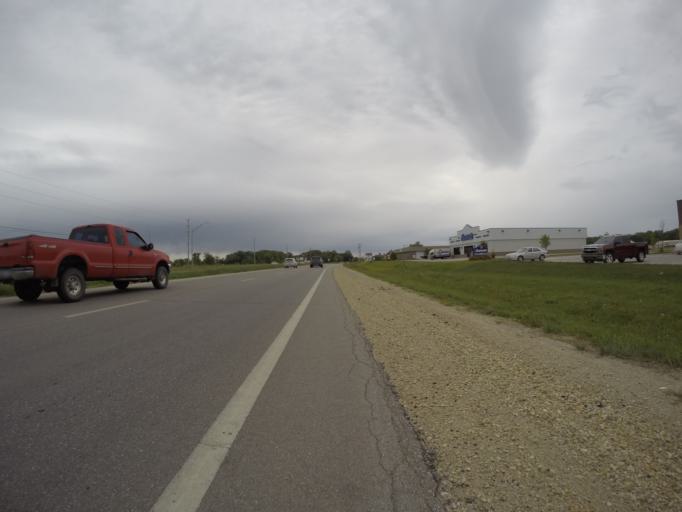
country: US
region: Kansas
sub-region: Riley County
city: Manhattan
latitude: 39.1951
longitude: -96.5244
